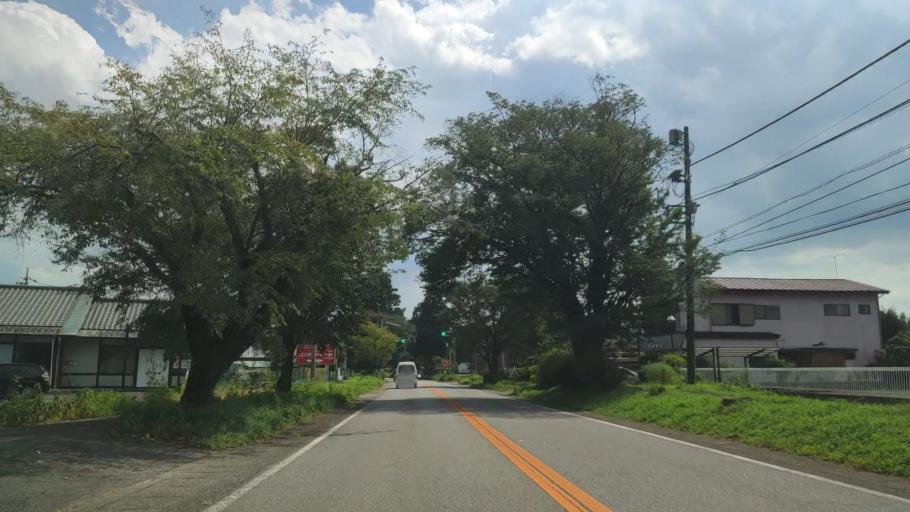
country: JP
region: Tochigi
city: Utsunomiya-shi
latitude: 36.6179
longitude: 139.8536
